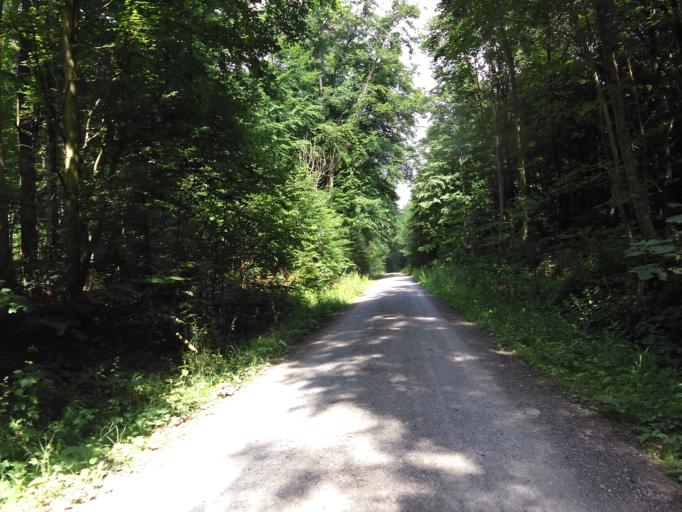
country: DE
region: Bavaria
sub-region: Regierungsbezirk Unterfranken
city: Wuerzburg
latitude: 49.7629
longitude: 9.9002
